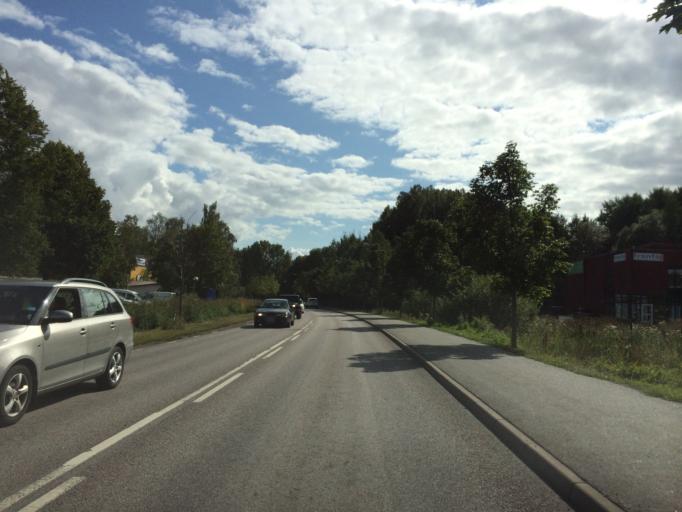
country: SE
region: Stockholm
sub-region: Sollentuna Kommun
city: Sollentuna
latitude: 59.4333
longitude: 17.9312
